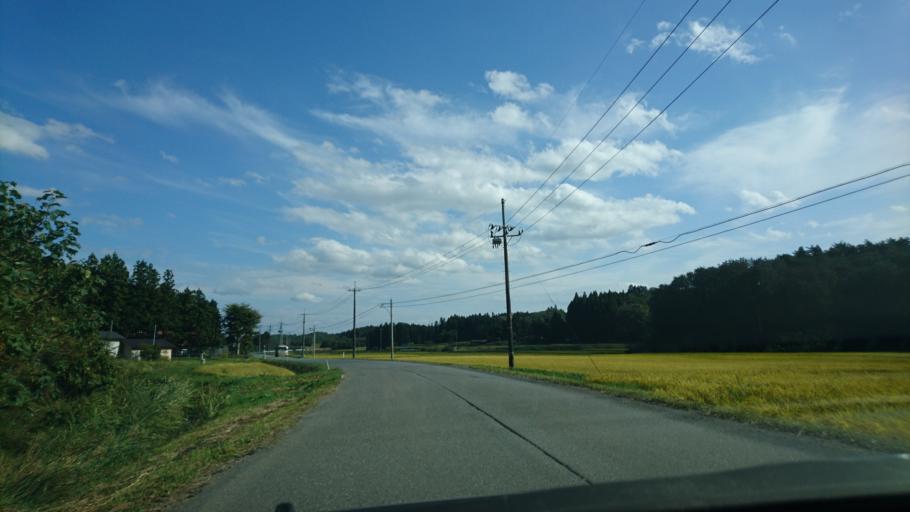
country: JP
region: Iwate
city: Ichinoseki
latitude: 38.8780
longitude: 141.0682
